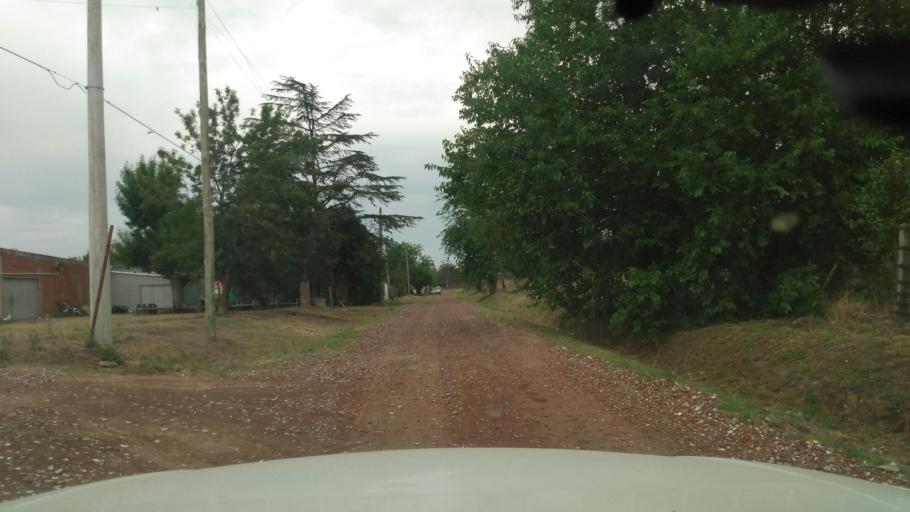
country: AR
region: Buenos Aires
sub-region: Partido de Lujan
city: Lujan
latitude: -34.5533
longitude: -59.2020
